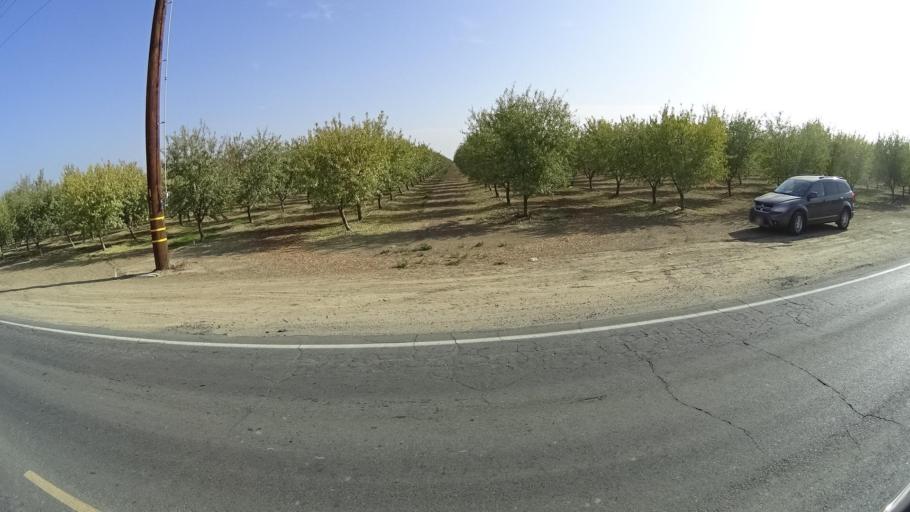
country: US
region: California
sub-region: Kern County
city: Delano
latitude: 35.7337
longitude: -119.2231
